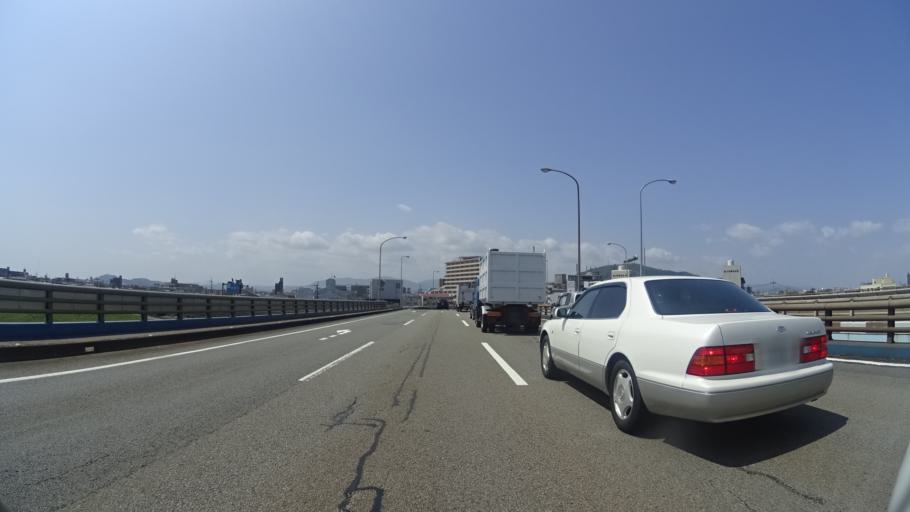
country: JP
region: Tokushima
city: Tokushima-shi
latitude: 34.0857
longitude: 134.5656
